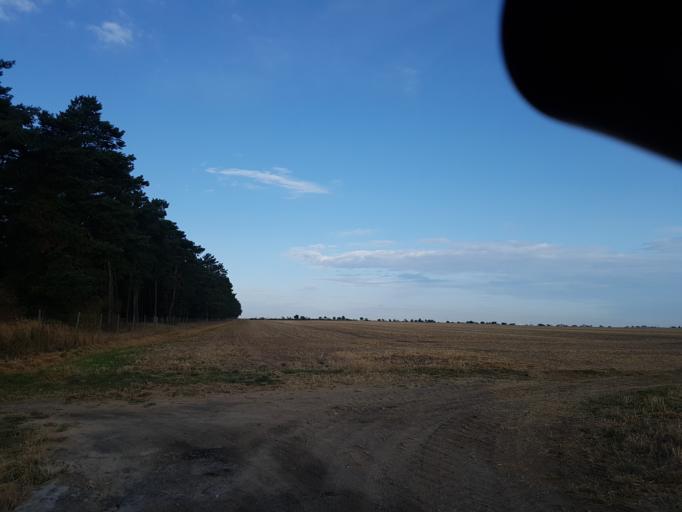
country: DE
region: Brandenburg
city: Niedergorsdorf
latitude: 51.9347
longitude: 13.0090
